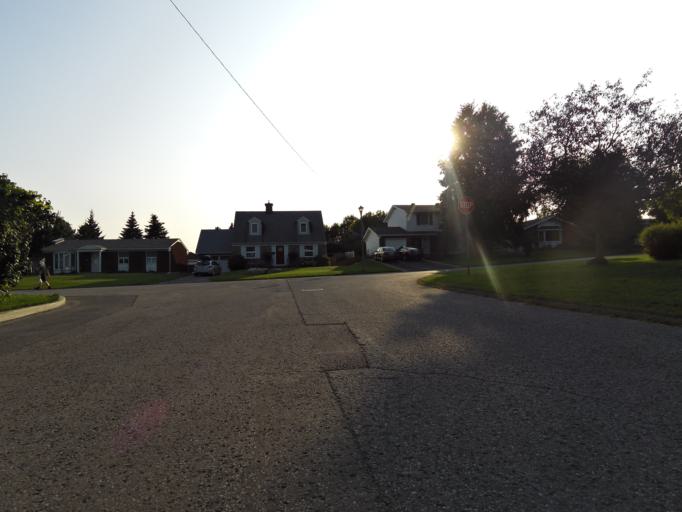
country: CA
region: Ontario
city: Bells Corners
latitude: 45.2970
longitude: -75.8862
